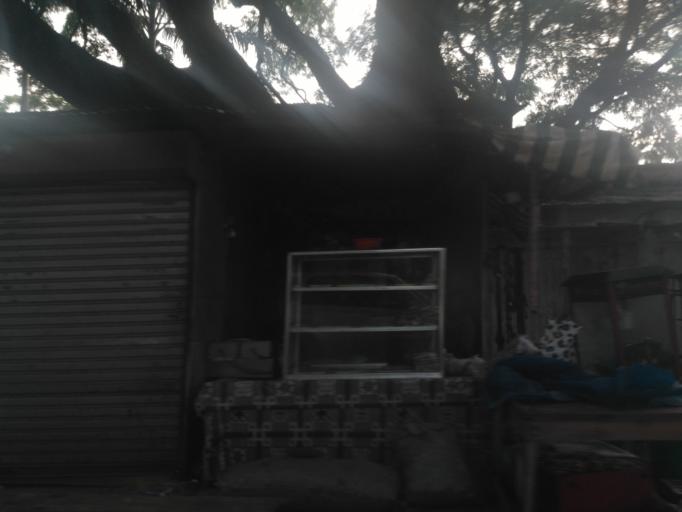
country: TZ
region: Zanzibar Urban/West
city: Zanzibar
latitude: -6.1634
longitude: 39.1941
